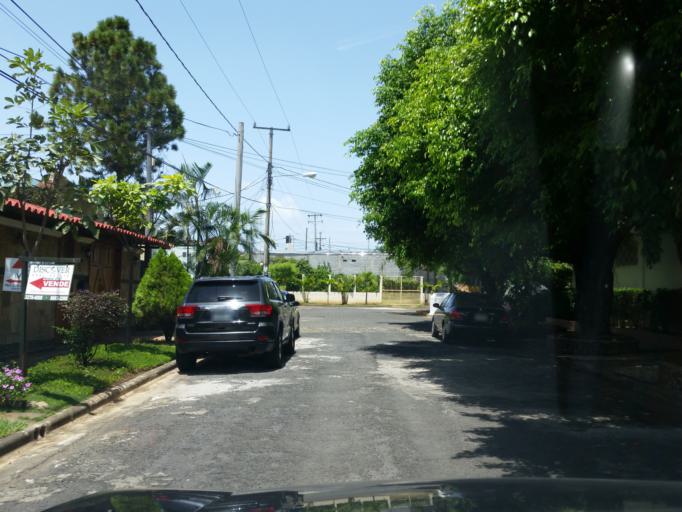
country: NI
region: Managua
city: Managua
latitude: 12.1046
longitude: -86.2637
